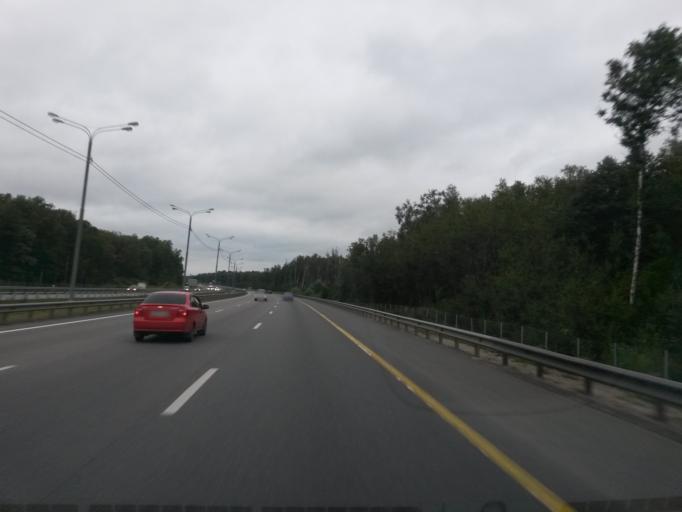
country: RU
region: Moskovskaya
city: Vostryakovo
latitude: 55.3555
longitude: 37.8020
